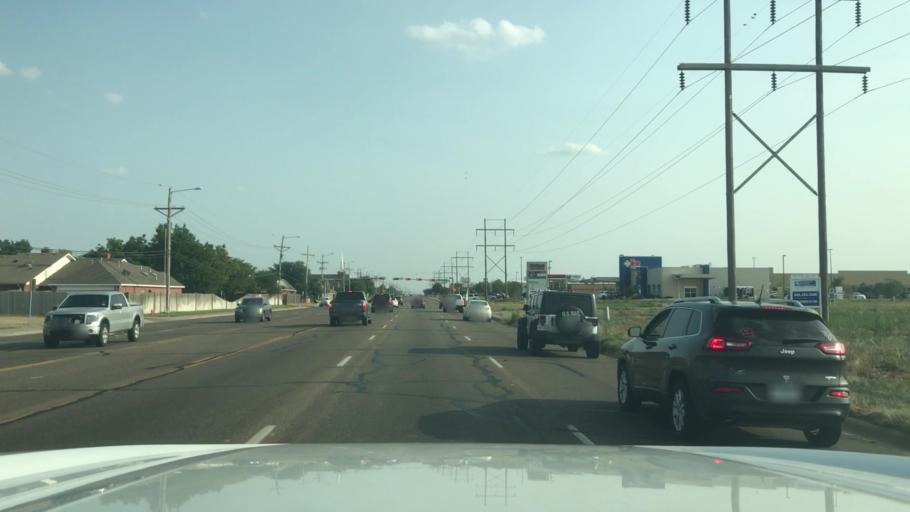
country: US
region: Texas
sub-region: Potter County
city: Amarillo
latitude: 35.1729
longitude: -101.9382
